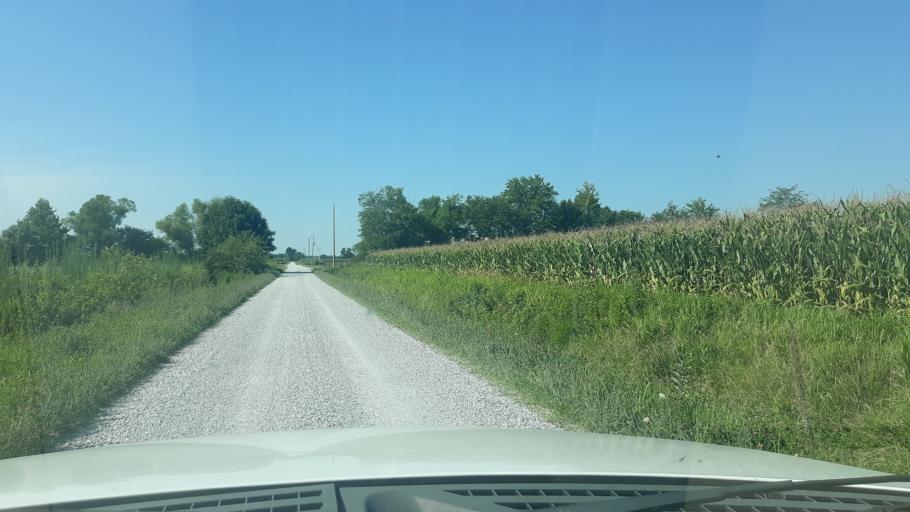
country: US
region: Illinois
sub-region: Saline County
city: Eldorado
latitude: 37.8499
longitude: -88.4849
